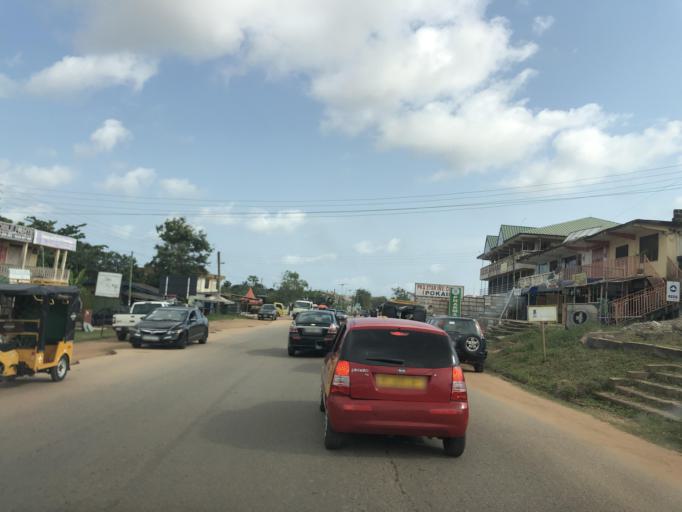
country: GH
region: Central
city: Cape Coast
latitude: 5.1416
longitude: -1.2830
